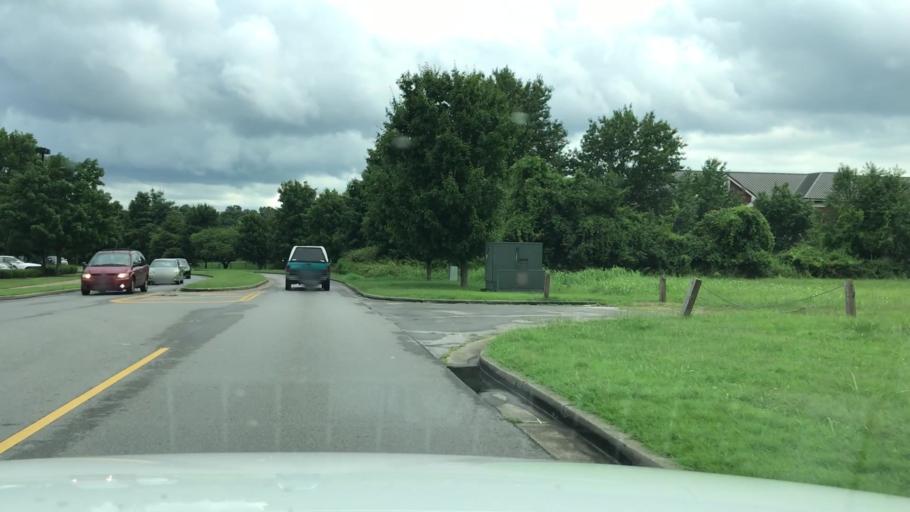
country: US
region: Tennessee
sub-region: Sumner County
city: Hendersonville
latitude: 36.3145
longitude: -86.5959
